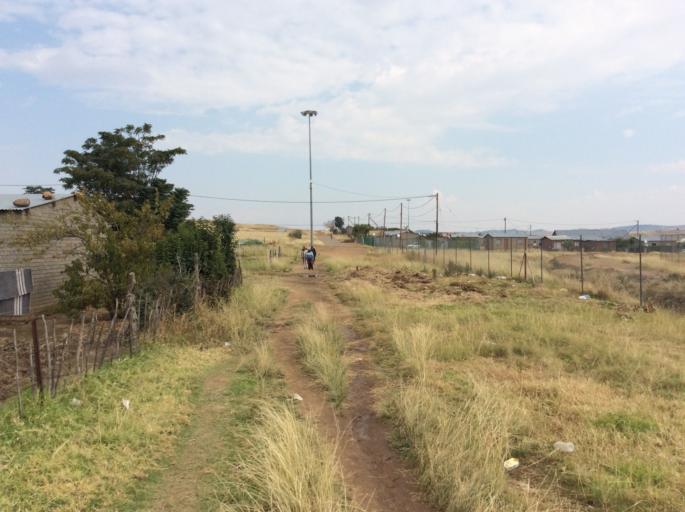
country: LS
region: Mafeteng
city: Mafeteng
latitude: -29.9851
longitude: 27.0079
